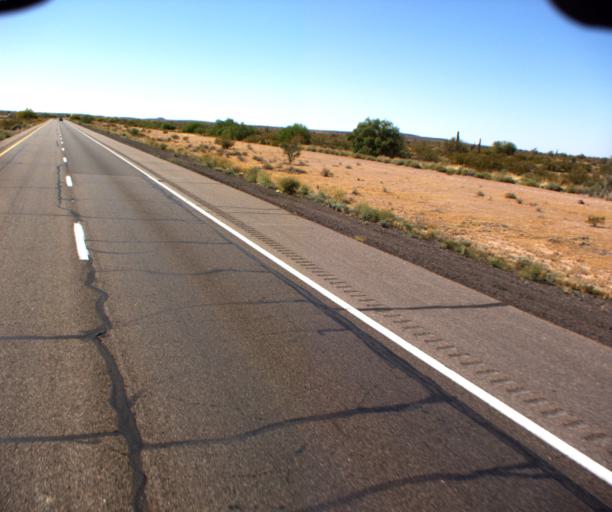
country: US
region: Arizona
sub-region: Maricopa County
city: Gila Bend
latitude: 32.8953
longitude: -113.0320
